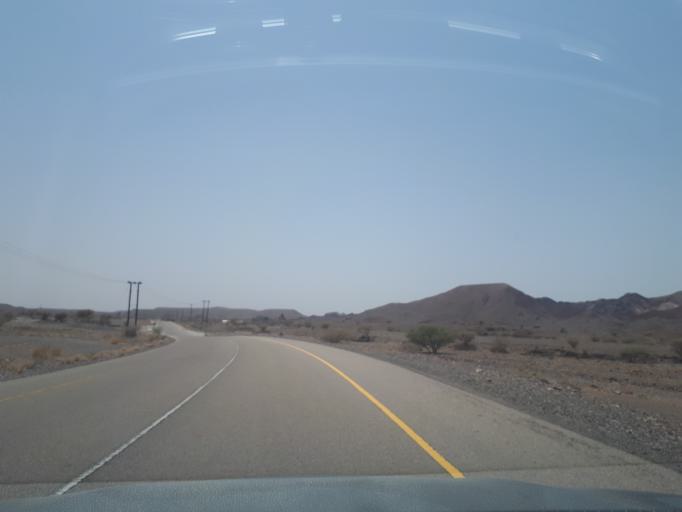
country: OM
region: Ash Sharqiyah
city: Badiyah
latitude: 22.4939
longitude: 59.0931
